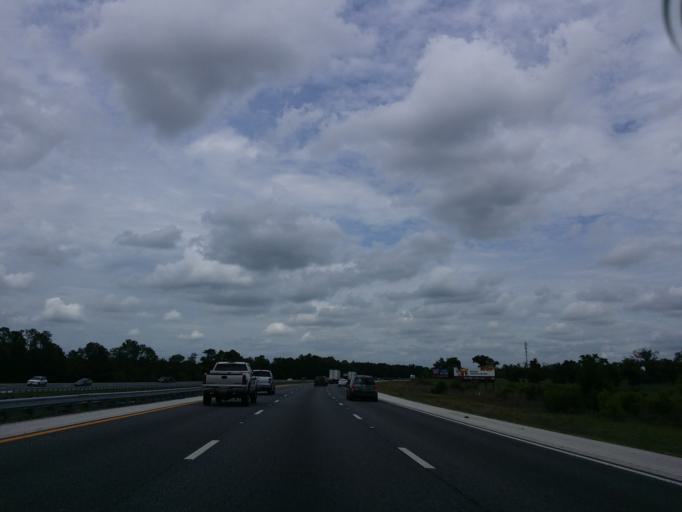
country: US
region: Florida
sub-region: Marion County
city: Ocala
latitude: 29.0766
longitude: -82.1838
